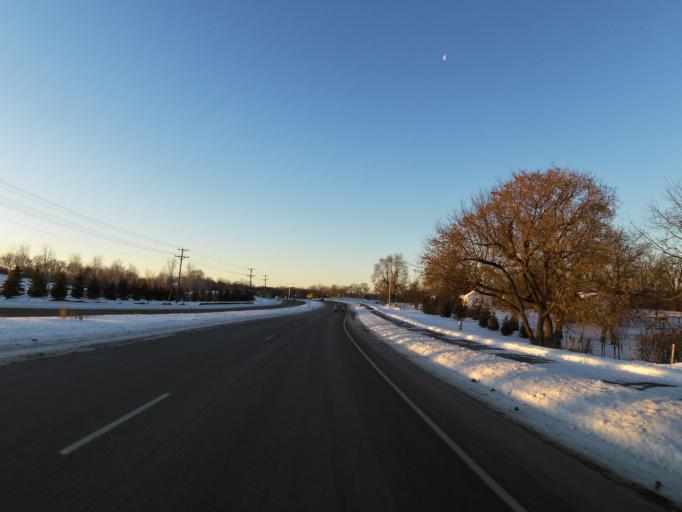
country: US
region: Minnesota
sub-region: Scott County
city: Prior Lake
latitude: 44.7206
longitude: -93.3770
